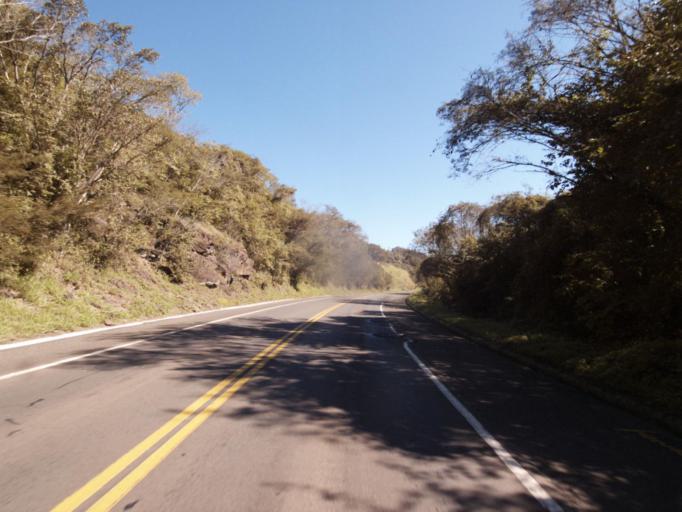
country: BR
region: Rio Grande do Sul
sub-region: Frederico Westphalen
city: Frederico Westphalen
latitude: -26.8253
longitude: -53.3978
